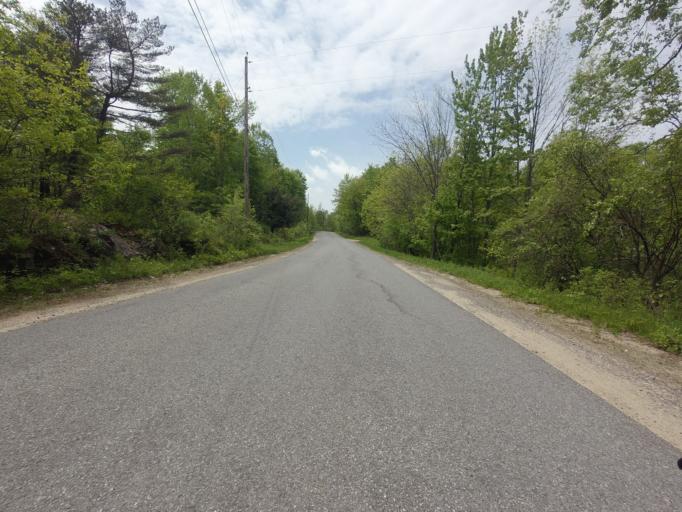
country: US
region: New York
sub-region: St. Lawrence County
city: Hannawa Falls
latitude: 44.5515
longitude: -74.9826
